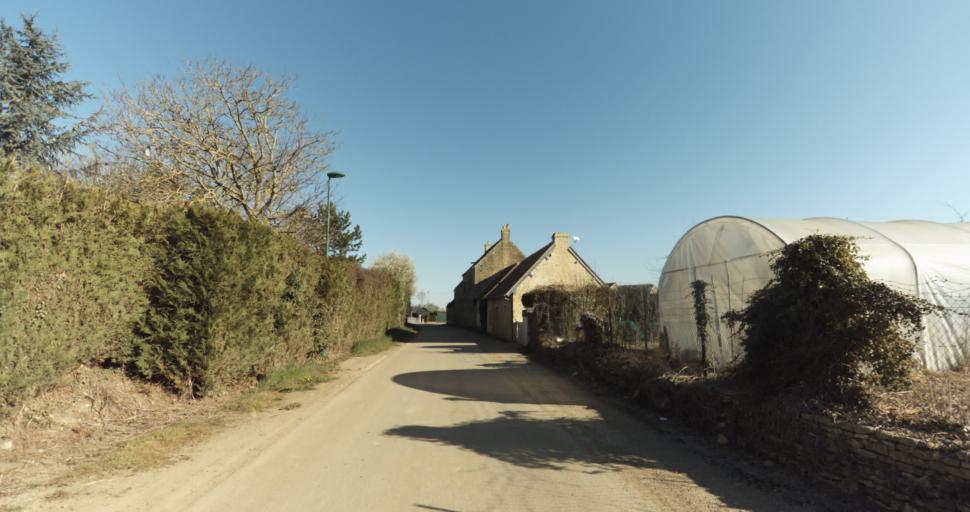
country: FR
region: Lower Normandy
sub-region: Departement du Calvados
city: Saint-Pierre-sur-Dives
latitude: 48.9889
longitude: -0.0247
